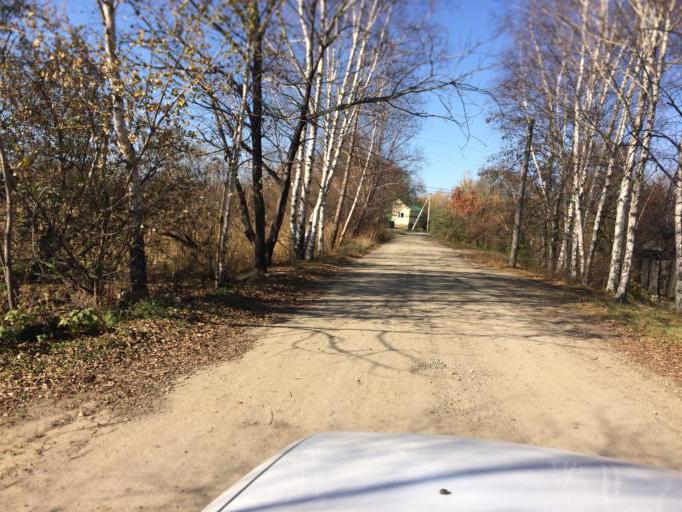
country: RU
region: Primorskiy
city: Dal'nerechensk
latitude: 45.9125
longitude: 133.8059
